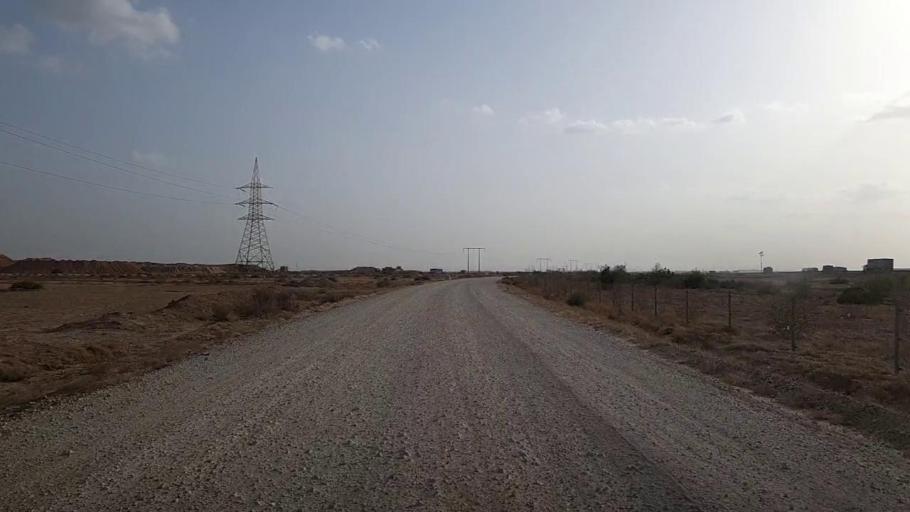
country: PK
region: Sindh
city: Thatta
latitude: 25.1994
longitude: 67.8803
